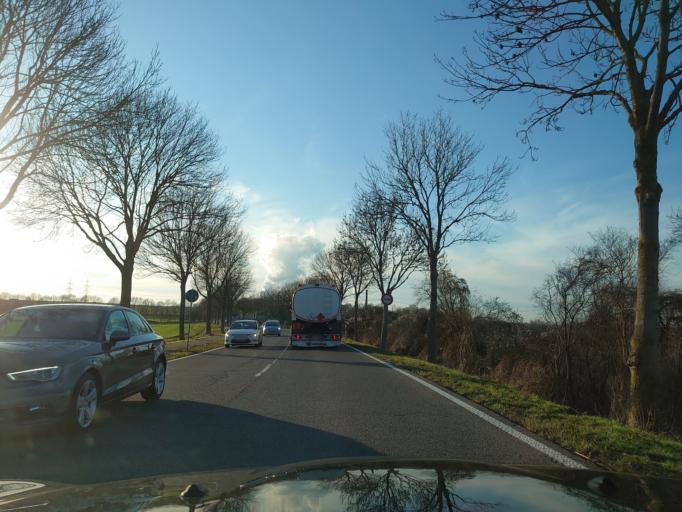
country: DE
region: North Rhine-Westphalia
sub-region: Regierungsbezirk Dusseldorf
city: Rommerskirchen
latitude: 51.0680
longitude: 6.7386
